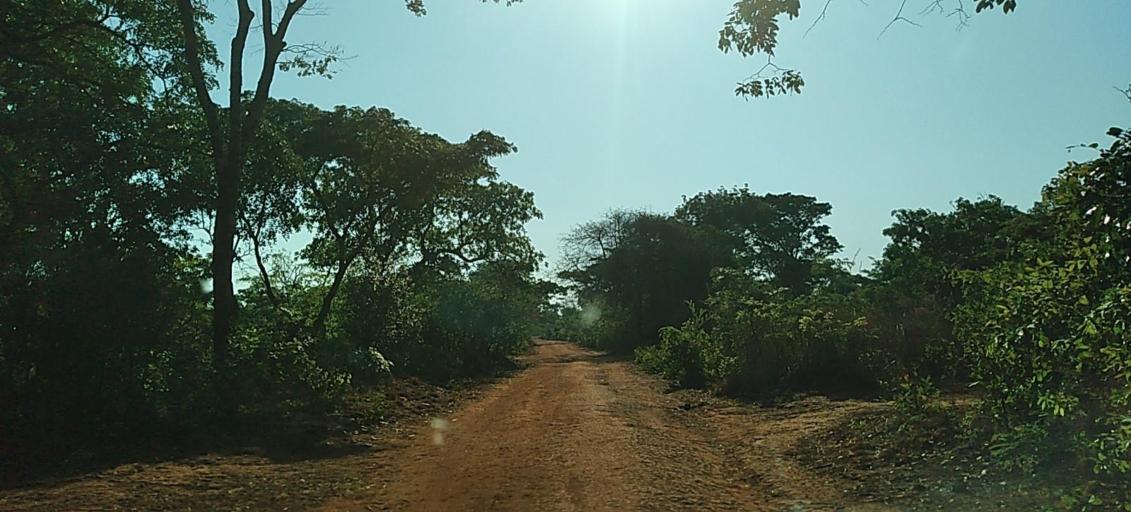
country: ZM
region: Copperbelt
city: Luanshya
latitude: -13.4592
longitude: 28.8107
